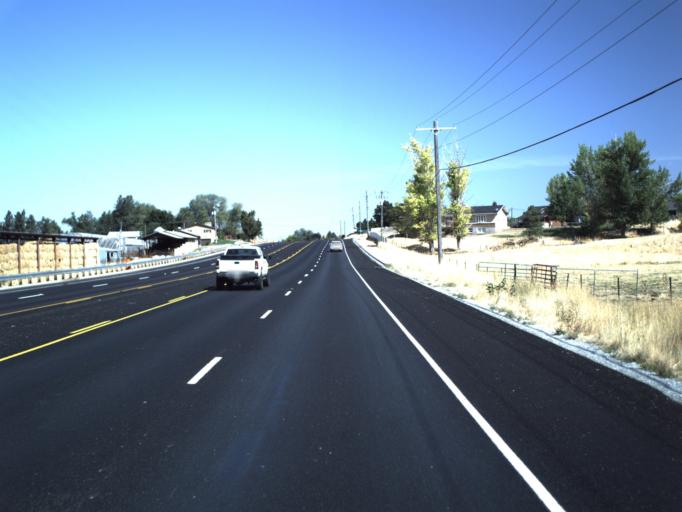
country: US
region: Utah
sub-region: Cache County
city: Nibley
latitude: 41.6547
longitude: -111.8327
